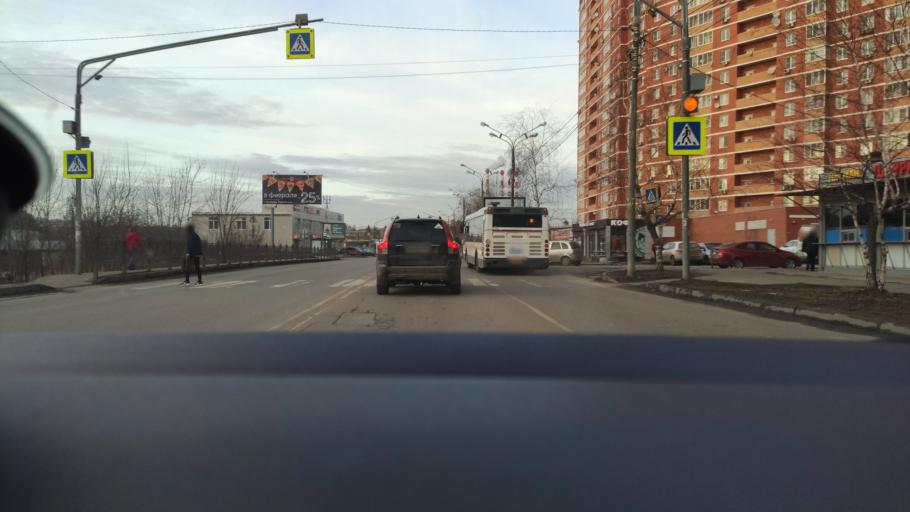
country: RU
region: Moskovskaya
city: Vidnoye
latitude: 55.5434
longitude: 37.7200
